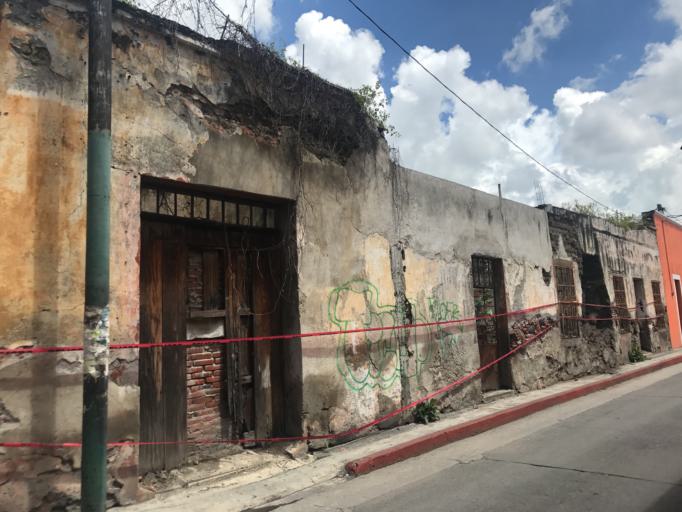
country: MX
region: Morelos
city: Cuautla Morelos
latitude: 18.8144
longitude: -98.9558
